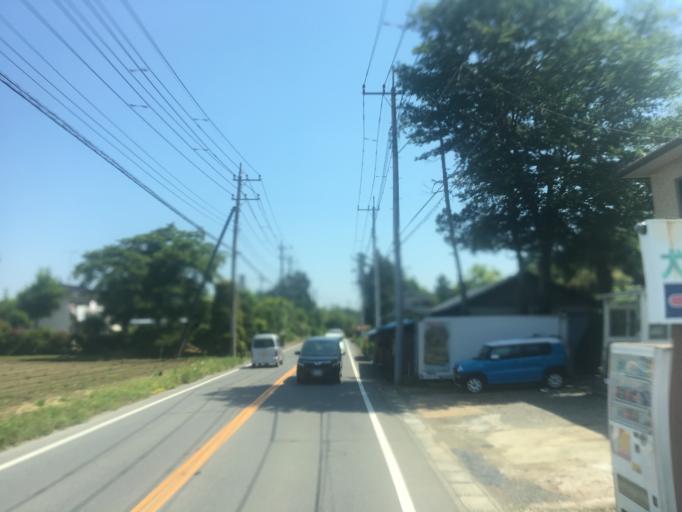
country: JP
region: Saitama
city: Ogawa
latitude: 36.0167
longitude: 139.3122
